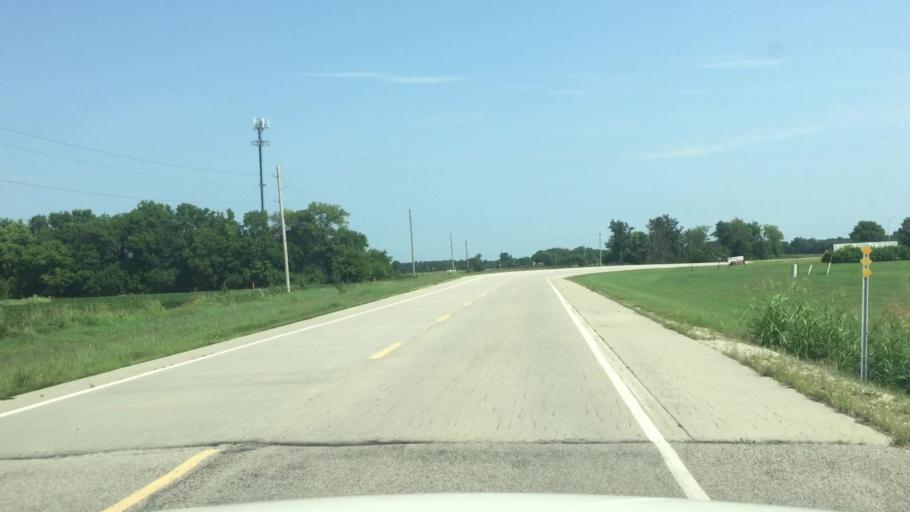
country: US
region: Kansas
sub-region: Montgomery County
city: Coffeyville
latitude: 37.1027
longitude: -95.5861
